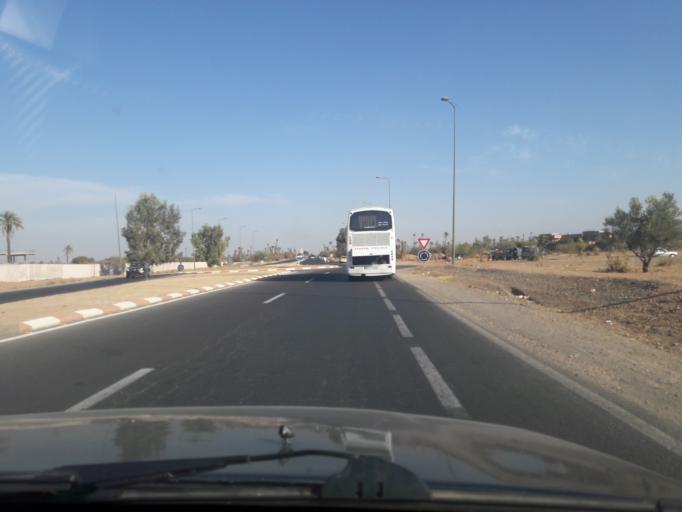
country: MA
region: Marrakech-Tensift-Al Haouz
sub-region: Marrakech
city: Marrakesh
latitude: 31.6476
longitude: -7.9175
